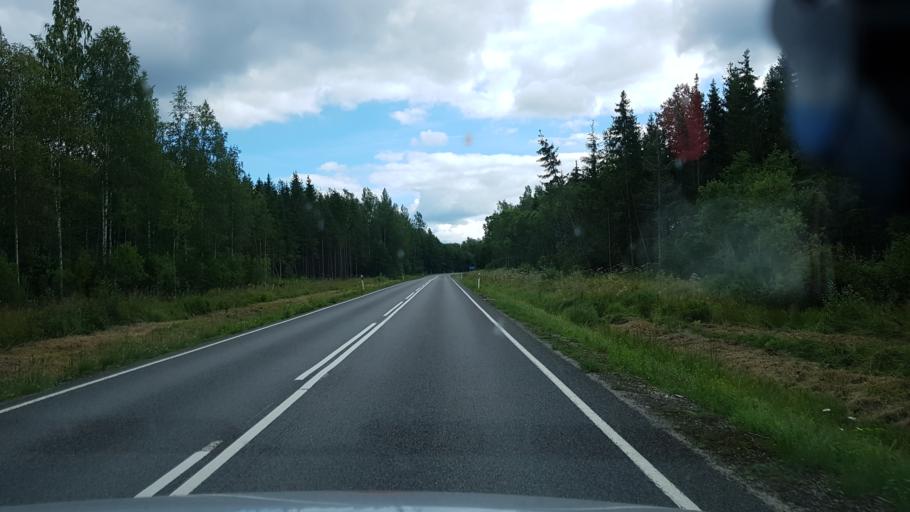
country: EE
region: Ida-Virumaa
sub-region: Kivioli linn
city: Kivioli
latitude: 59.1483
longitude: 26.8956
